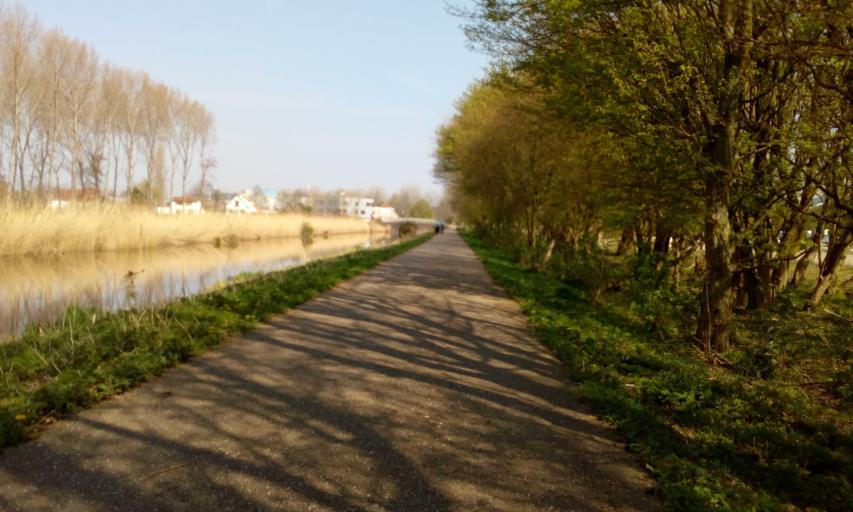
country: NL
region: South Holland
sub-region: Gemeente Spijkenisse
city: Spijkenisse
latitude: 51.8450
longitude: 4.3087
